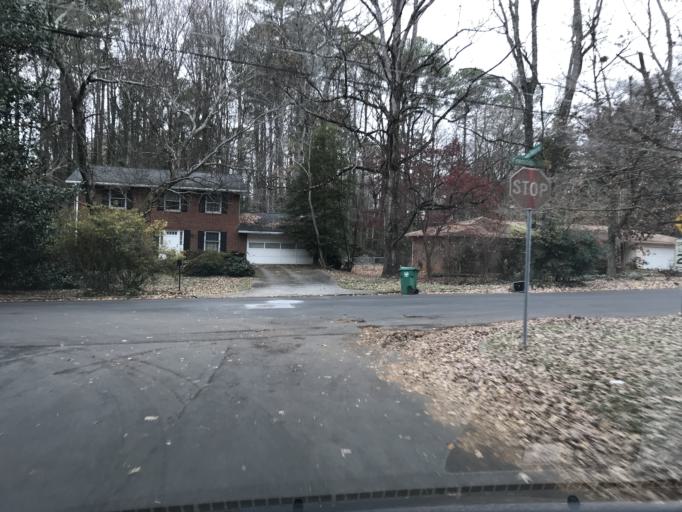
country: US
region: Georgia
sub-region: DeKalb County
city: Clarkston
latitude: 33.8156
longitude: -84.2561
